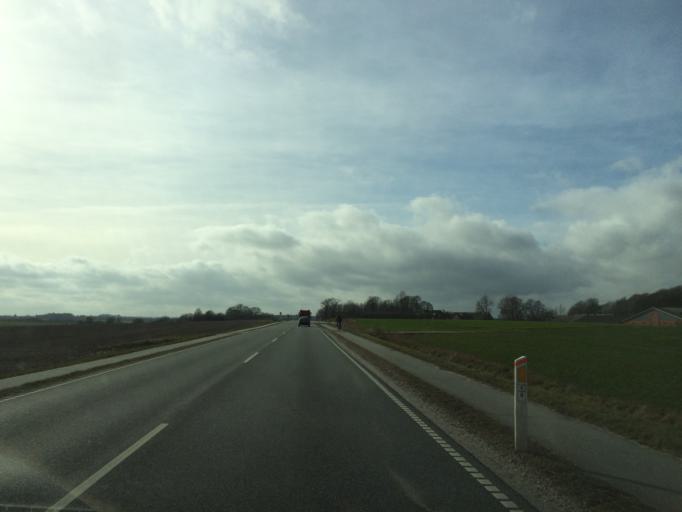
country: DK
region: Central Jutland
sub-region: Randers Kommune
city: Randers
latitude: 56.4707
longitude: 9.9625
